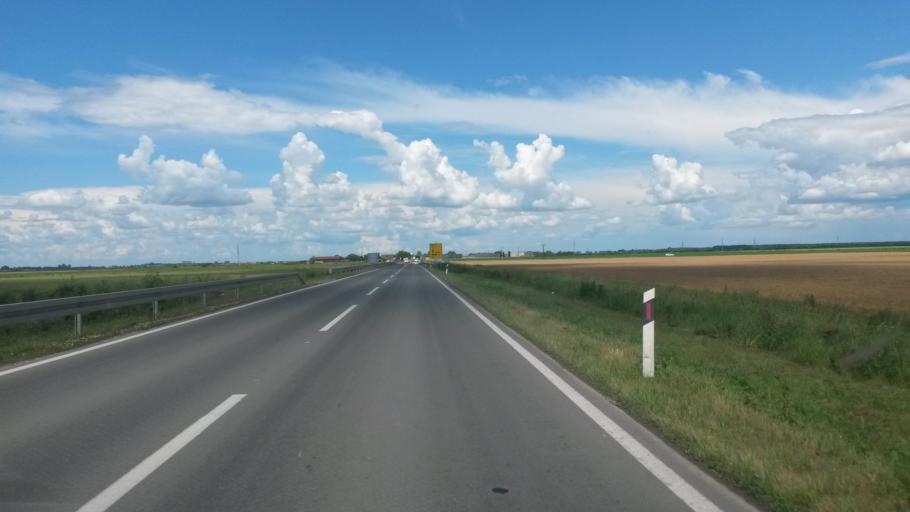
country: HR
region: Osjecko-Baranjska
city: Ovcara
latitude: 45.4861
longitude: 18.5459
